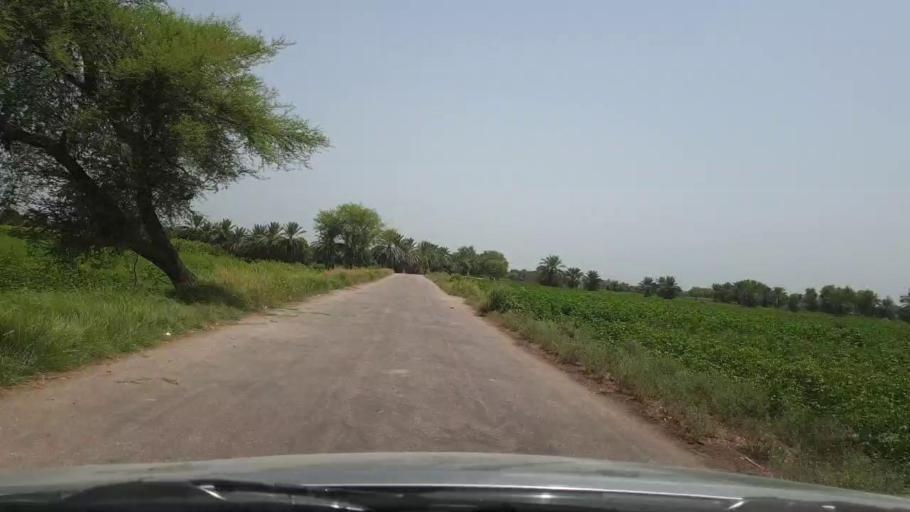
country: PK
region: Sindh
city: Pano Aqil
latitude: 27.8782
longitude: 69.1475
